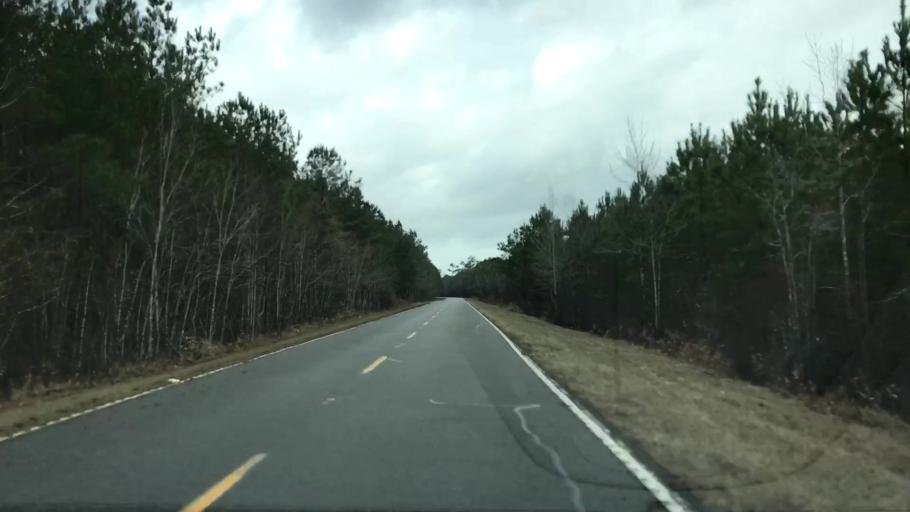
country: US
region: South Carolina
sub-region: Georgetown County
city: Murrells Inlet
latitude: 33.6295
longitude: -79.2465
